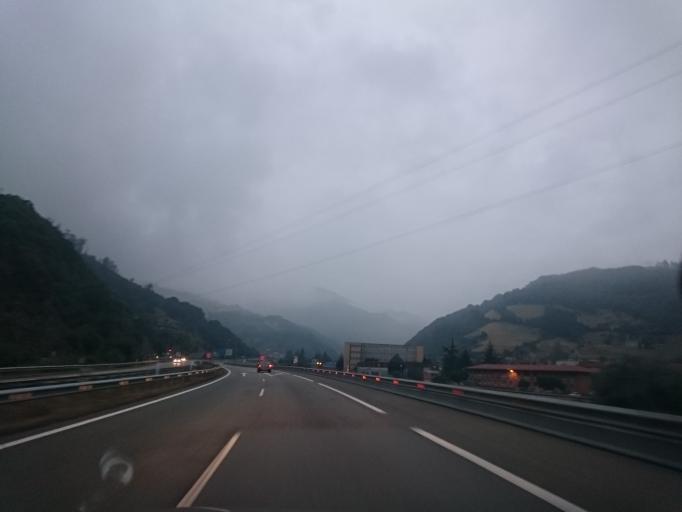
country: ES
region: Asturias
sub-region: Province of Asturias
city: Mieres
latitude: 43.2073
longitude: -5.7876
